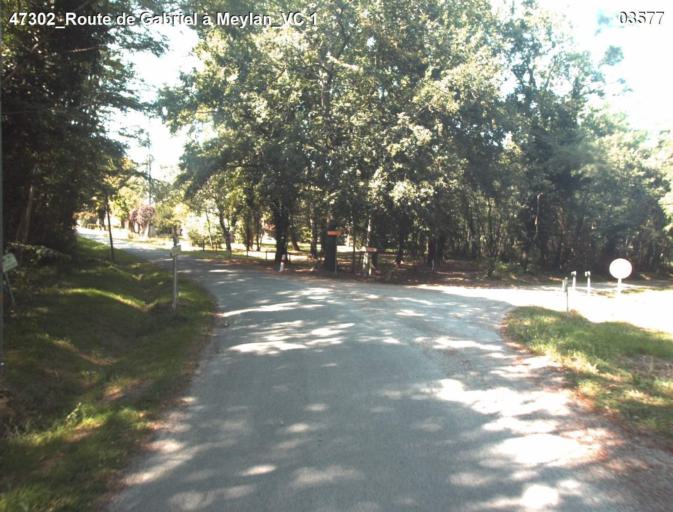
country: FR
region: Aquitaine
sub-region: Departement du Lot-et-Garonne
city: Mezin
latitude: 44.0749
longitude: 0.1213
